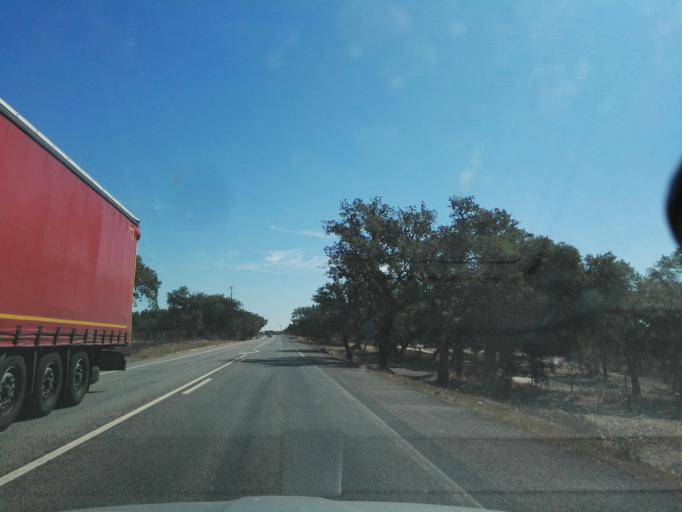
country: PT
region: Santarem
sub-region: Benavente
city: Poceirao
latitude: 38.8449
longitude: -8.7511
